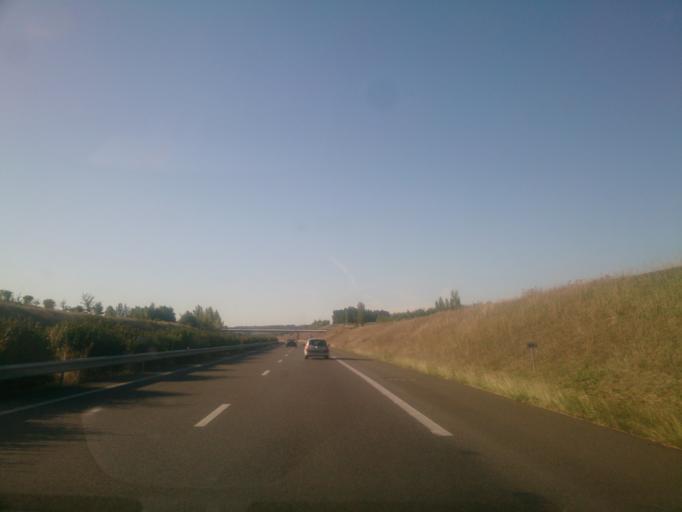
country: FR
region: Midi-Pyrenees
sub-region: Departement du Tarn-et-Garonne
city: Caussade
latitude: 44.2218
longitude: 1.5380
